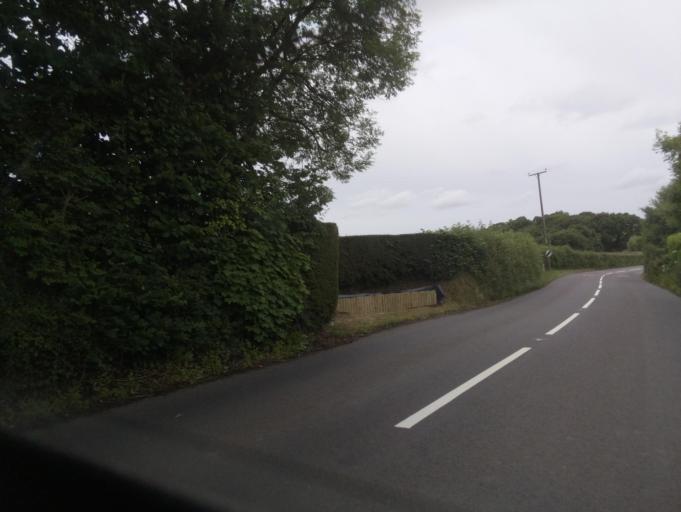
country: GB
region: England
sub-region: Devon
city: Crediton
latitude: 50.7060
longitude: -3.6133
